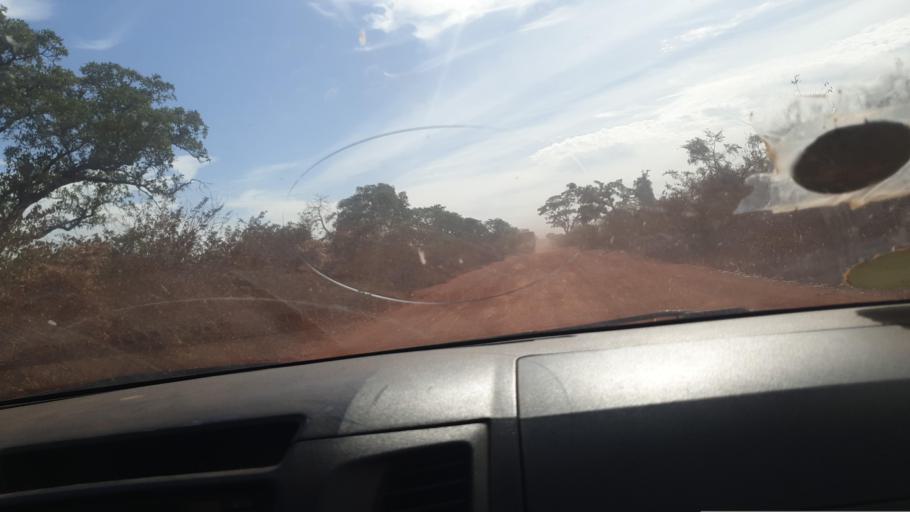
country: ML
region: Sikasso
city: Sikasso
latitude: 11.7572
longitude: -5.9661
